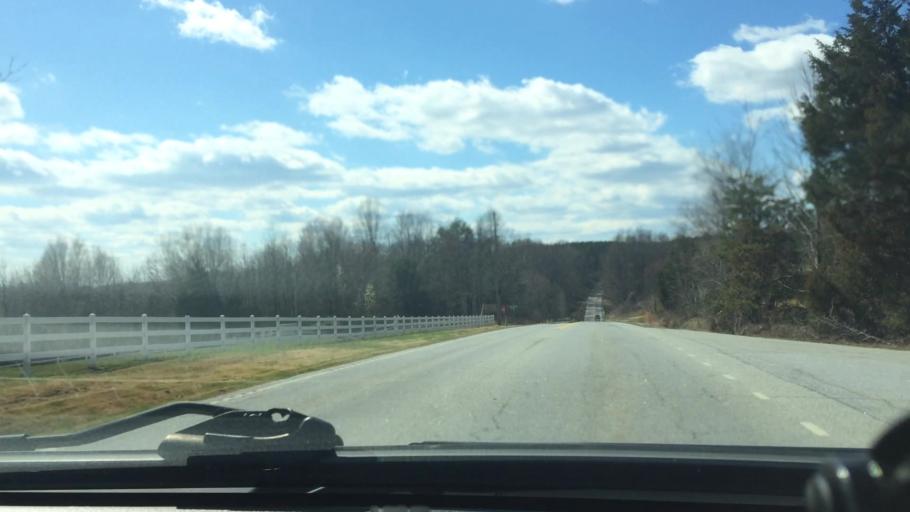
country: US
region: South Carolina
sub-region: Pickens County
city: Easley
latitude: 34.8911
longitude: -82.5627
